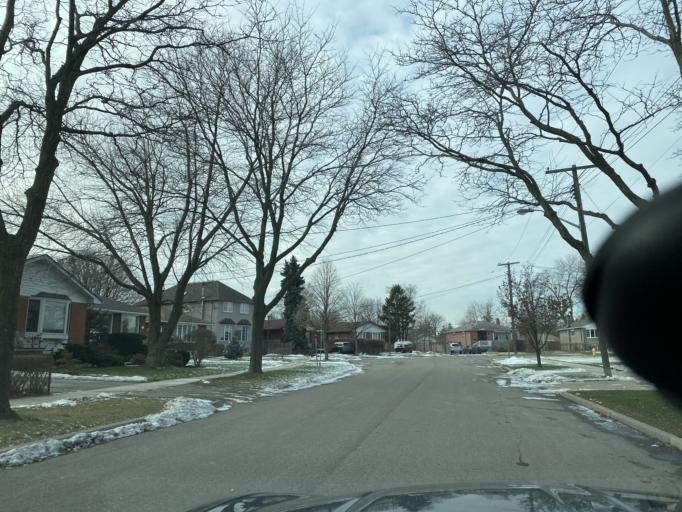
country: CA
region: Ontario
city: Etobicoke
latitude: 43.6643
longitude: -79.5756
